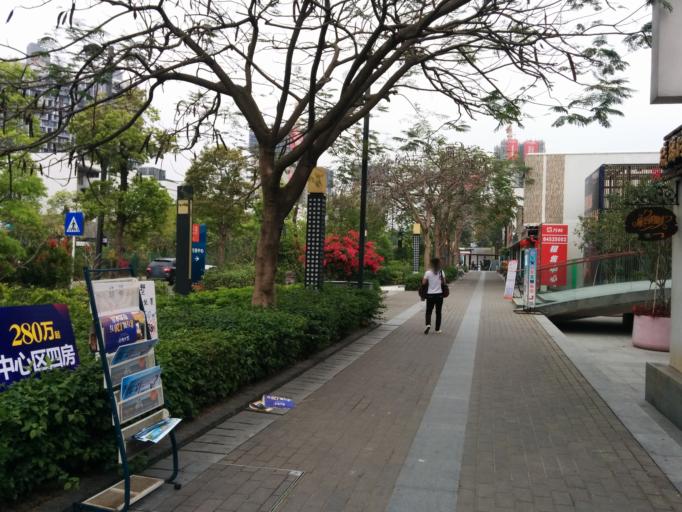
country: CN
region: Guangdong
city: Bantian
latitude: 22.6193
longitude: 114.0642
